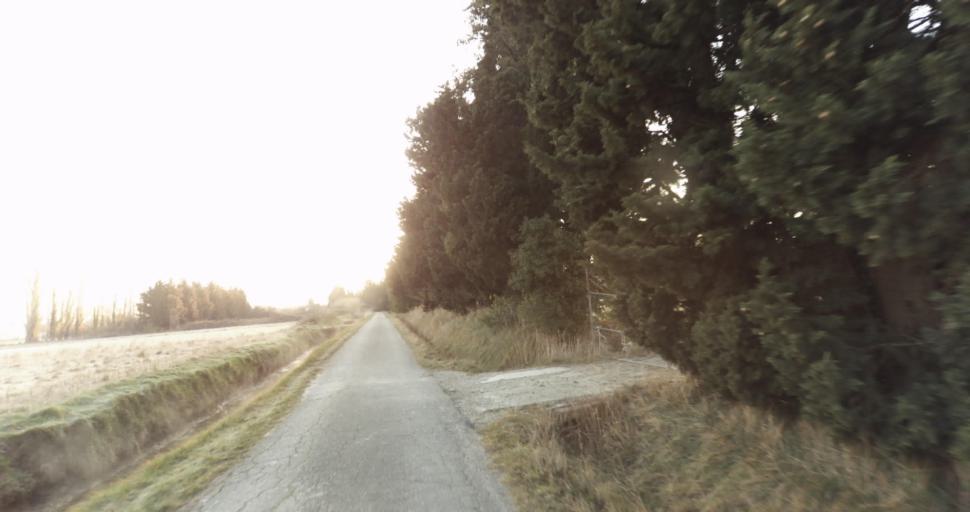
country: FR
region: Provence-Alpes-Cote d'Azur
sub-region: Departement des Bouches-du-Rhone
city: Rognonas
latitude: 43.8996
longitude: 4.7785
